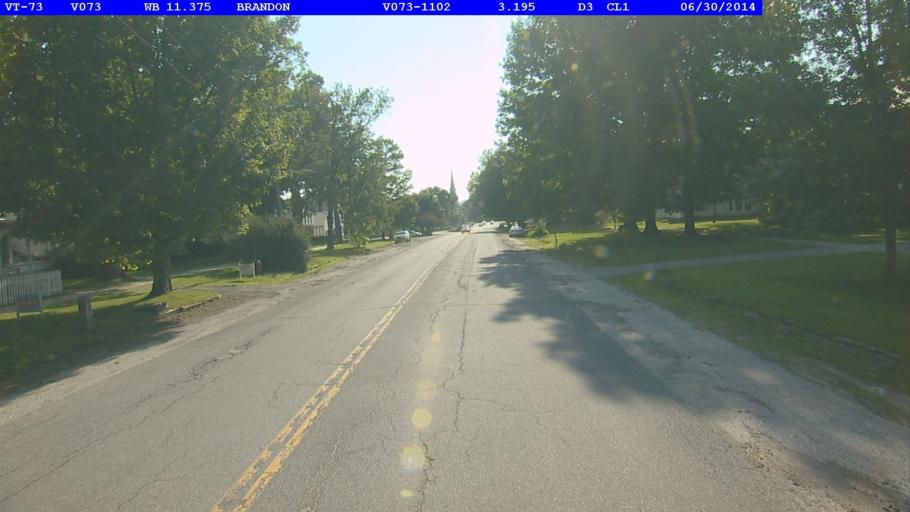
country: US
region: Vermont
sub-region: Rutland County
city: Brandon
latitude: 43.7985
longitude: -73.0841
